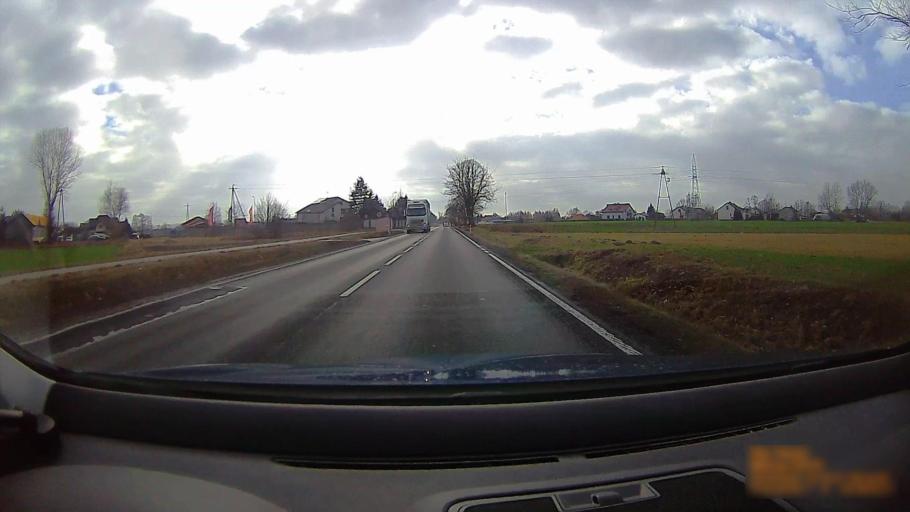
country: PL
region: Greater Poland Voivodeship
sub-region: Powiat koninski
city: Rychwal
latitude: 52.0830
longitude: 18.1619
